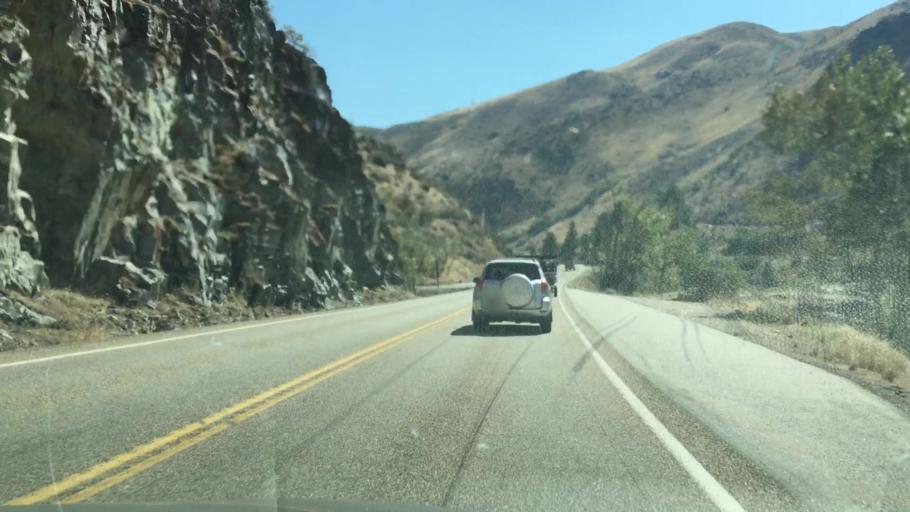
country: US
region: Idaho
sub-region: Ada County
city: Eagle
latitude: 43.9484
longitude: -116.1930
